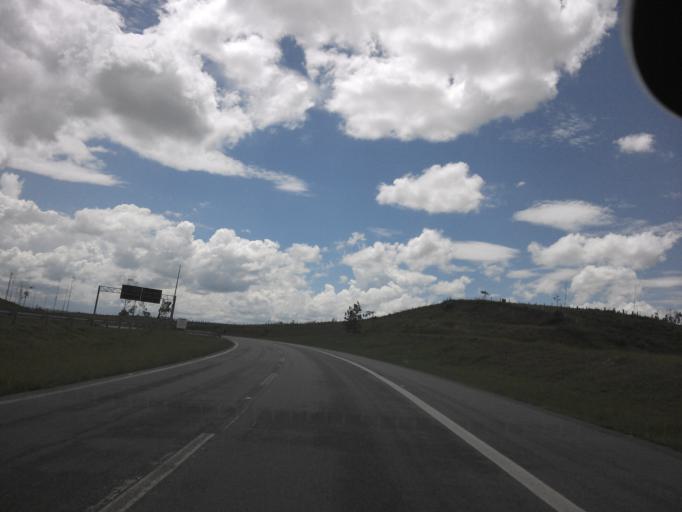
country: BR
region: Sao Paulo
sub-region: Jacarei
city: Jacarei
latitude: -23.3308
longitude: -46.0238
